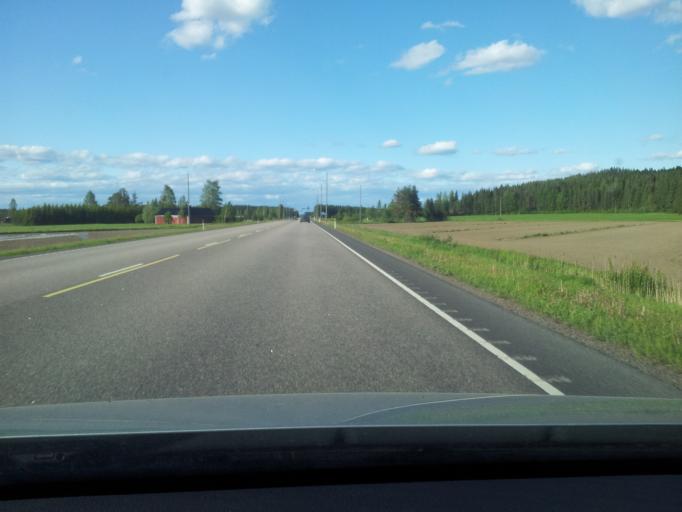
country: FI
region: Kymenlaakso
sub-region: Kouvola
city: Elimaeki
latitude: 60.7675
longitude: 26.4743
